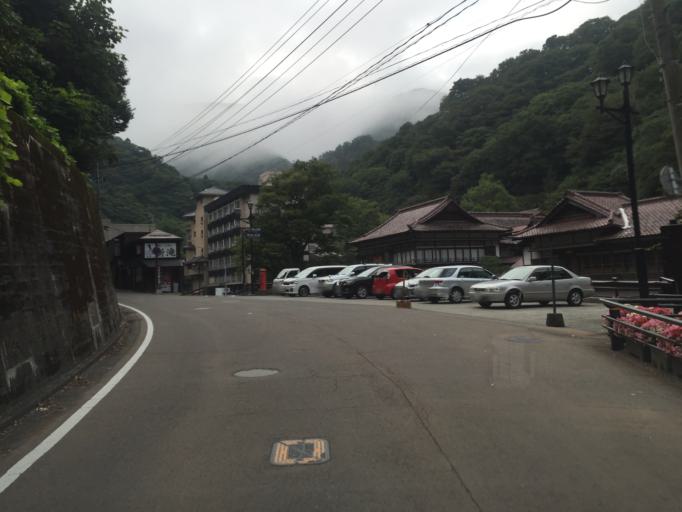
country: JP
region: Fukushima
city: Inawashiro
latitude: 37.4786
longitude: 139.9607
